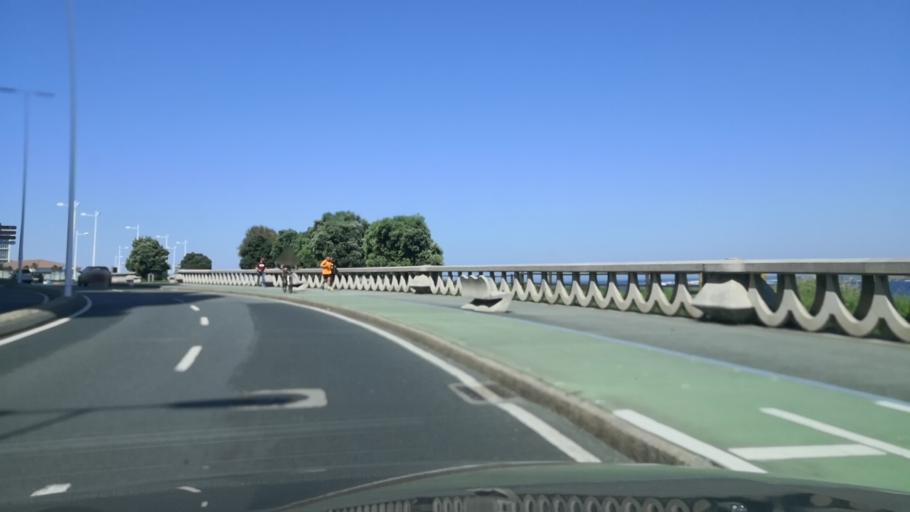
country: ES
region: Galicia
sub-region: Provincia da Coruna
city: A Coruna
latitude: 43.3729
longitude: -8.4192
